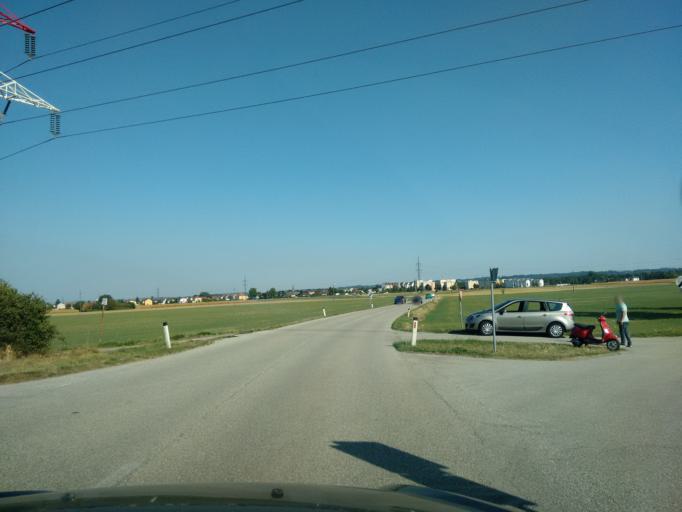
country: AT
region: Upper Austria
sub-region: Politischer Bezirk Linz-Land
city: Traun
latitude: 48.2221
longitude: 14.2096
